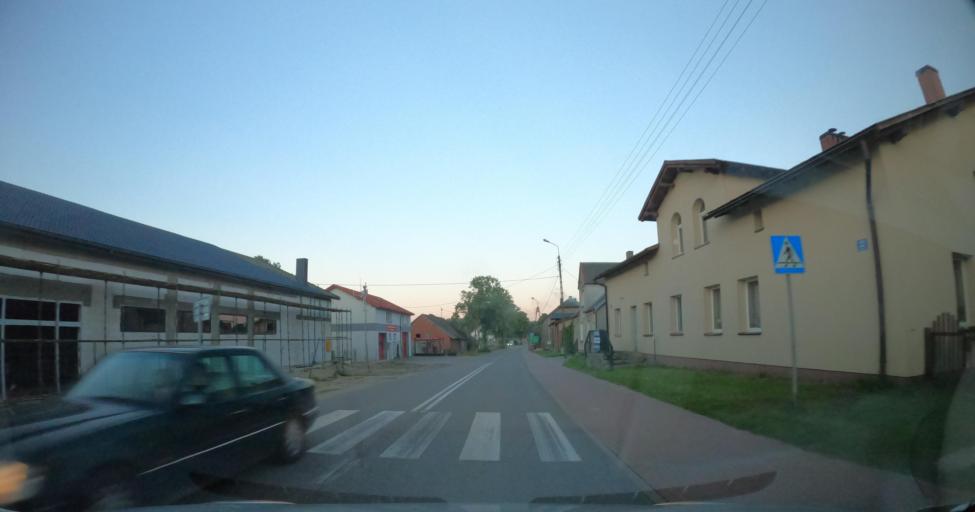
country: PL
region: Pomeranian Voivodeship
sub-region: Powiat wejherowski
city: Linia
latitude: 54.4552
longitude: 18.0260
